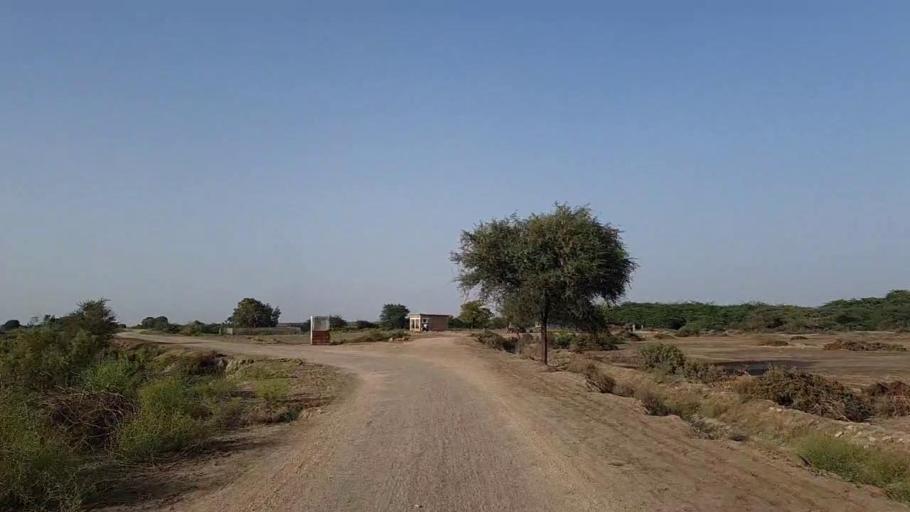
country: PK
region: Sindh
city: Jati
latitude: 24.3123
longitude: 68.1690
